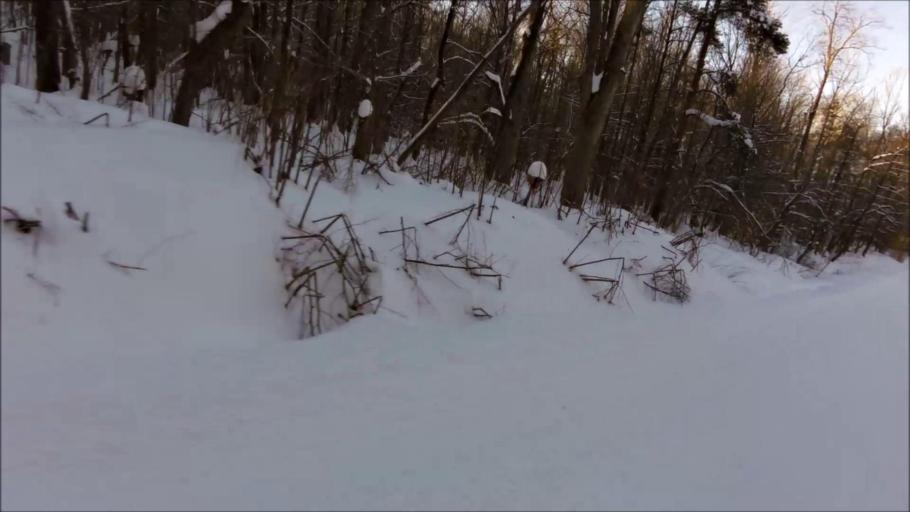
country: US
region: New York
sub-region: Chautauqua County
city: Mayville
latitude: 42.2716
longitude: -79.3821
